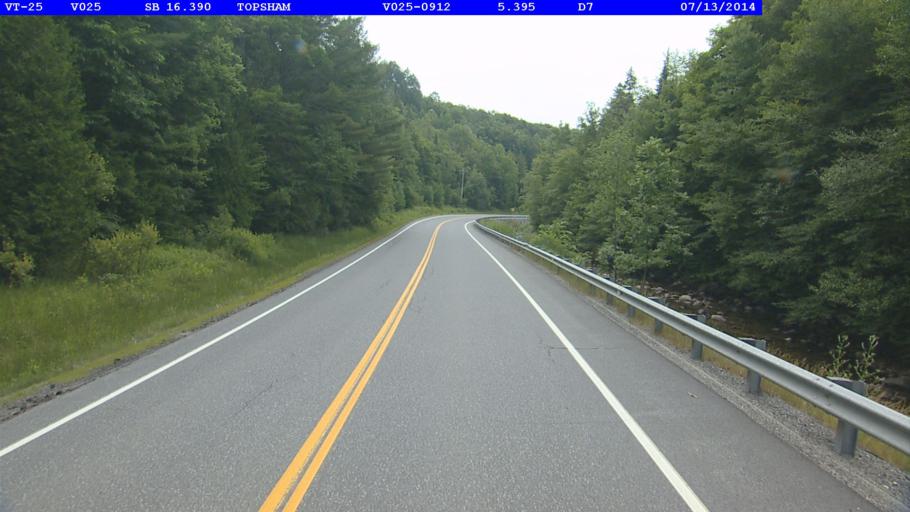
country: US
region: Vermont
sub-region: Orange County
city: Chelsea
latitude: 44.1241
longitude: -72.3069
